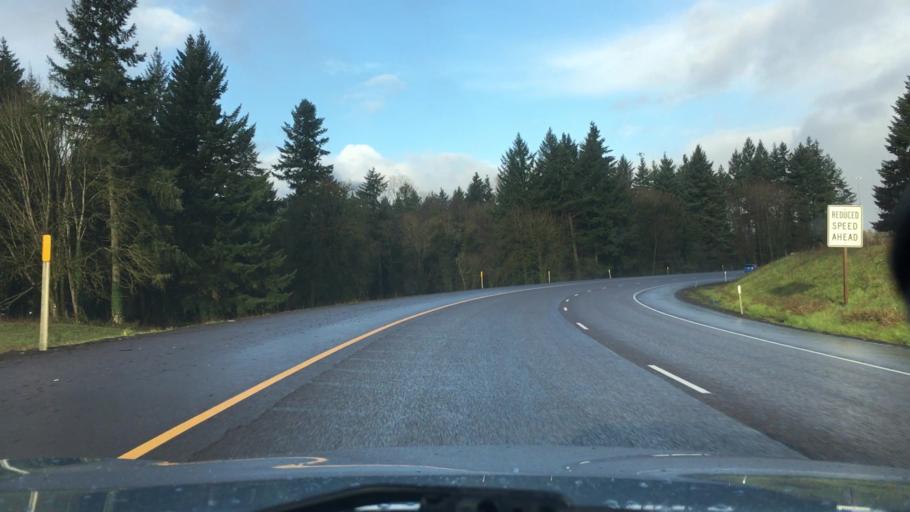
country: US
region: Oregon
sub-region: Washington County
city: Tualatin
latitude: 45.3703
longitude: -122.7530
